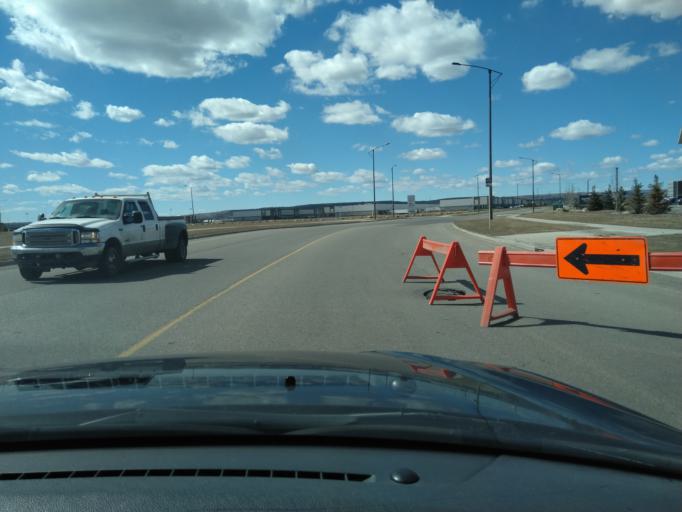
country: CA
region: Alberta
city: Calgary
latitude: 51.1367
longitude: -114.0263
